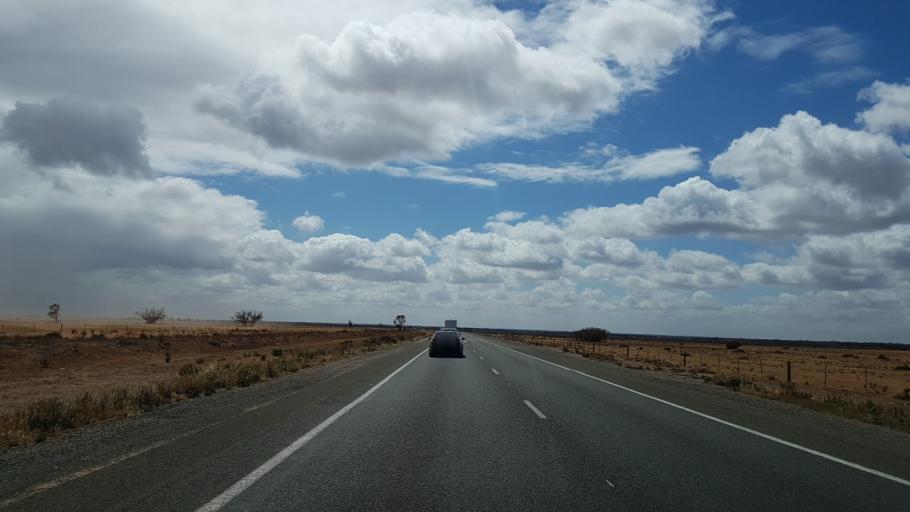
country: AU
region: South Australia
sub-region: Barossa
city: Angaston
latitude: -34.3935
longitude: 139.3273
